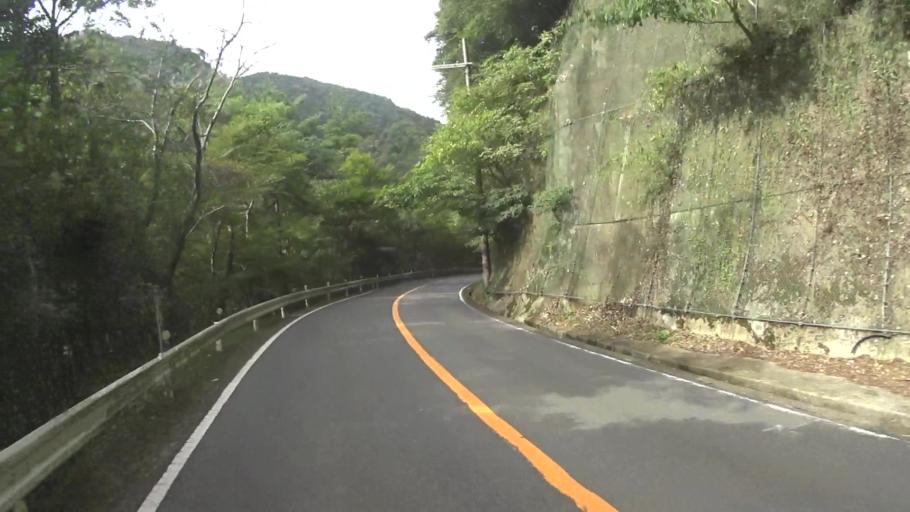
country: JP
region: Kyoto
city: Uji
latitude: 34.8861
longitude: 135.8609
